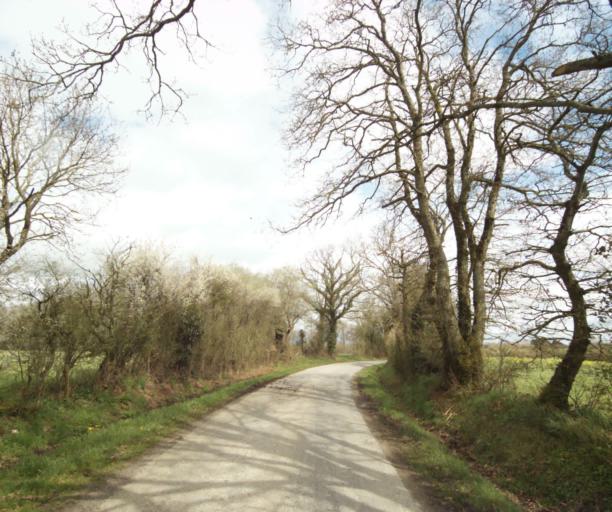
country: FR
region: Pays de la Loire
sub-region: Departement de la Loire-Atlantique
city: Bouvron
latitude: 47.4375
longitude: -1.8466
